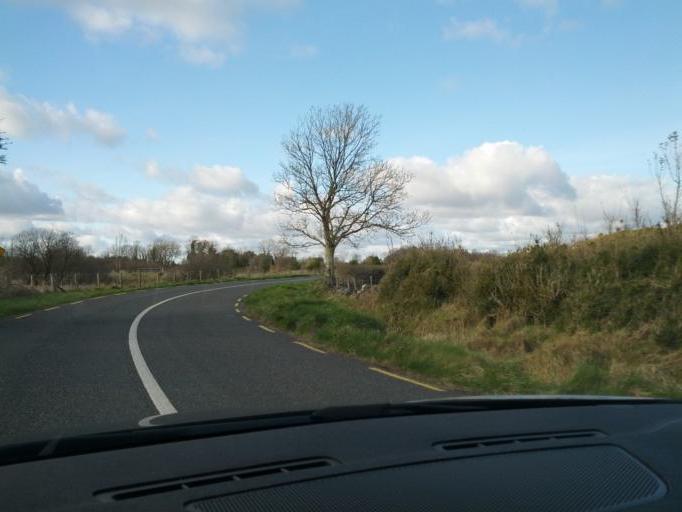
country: IE
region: Connaught
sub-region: County Galway
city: Athenry
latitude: 53.5043
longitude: -8.5723
